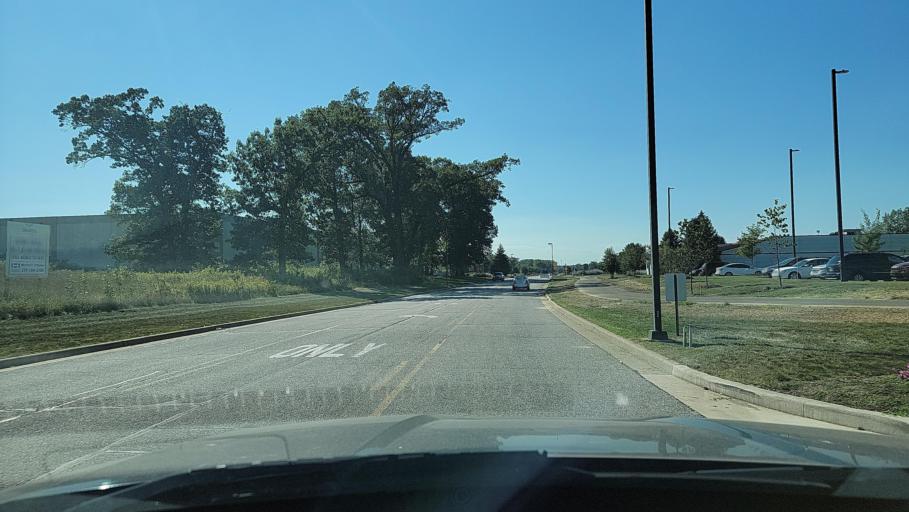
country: US
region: Indiana
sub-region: Porter County
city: Ogden Dunes
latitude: 41.6074
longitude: -87.1647
